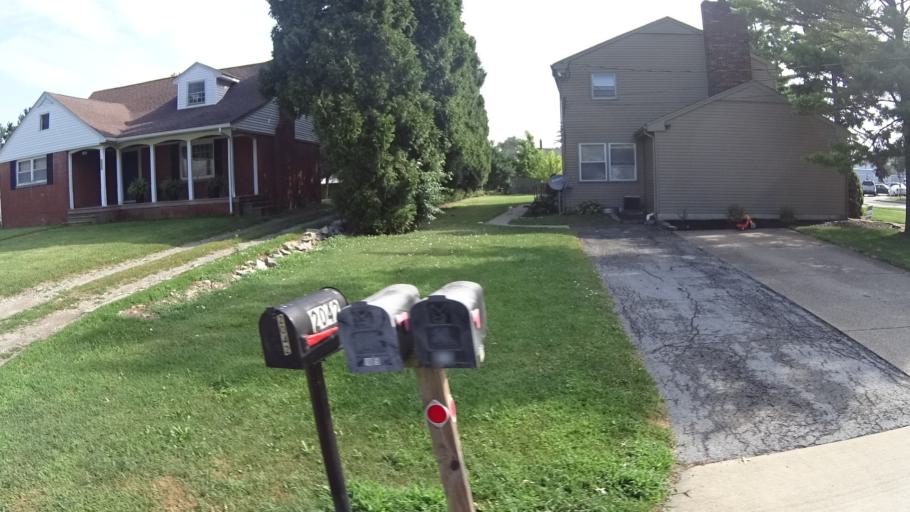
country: US
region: Ohio
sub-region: Erie County
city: Sandusky
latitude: 41.4370
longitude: -82.6735
